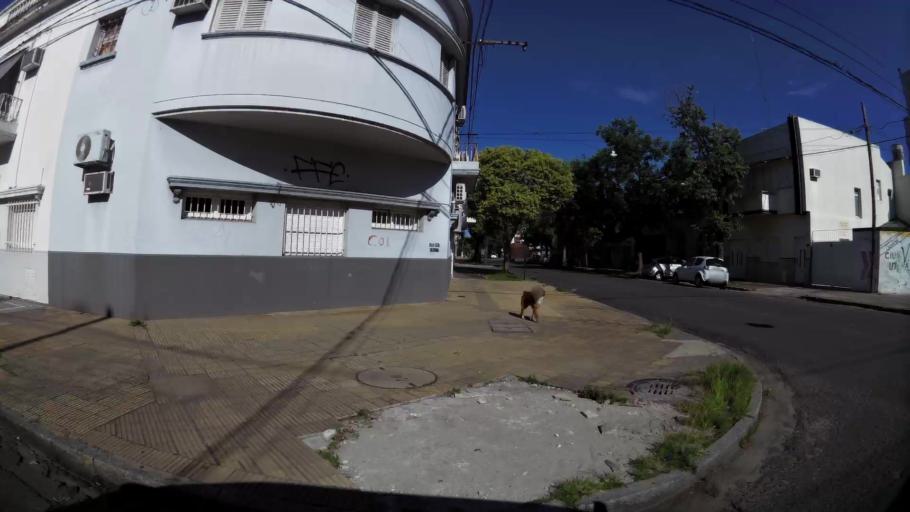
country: AR
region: Santa Fe
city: Santa Fe de la Vera Cruz
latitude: -31.6366
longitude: -60.7147
